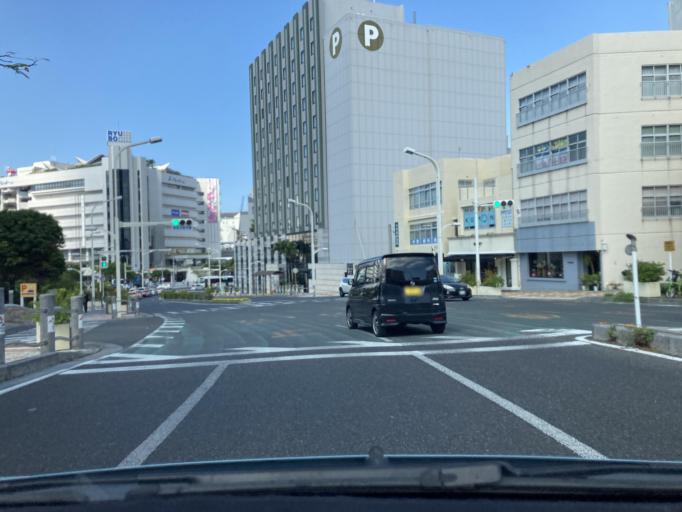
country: JP
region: Okinawa
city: Naha-shi
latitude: 26.2129
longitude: 127.6818
